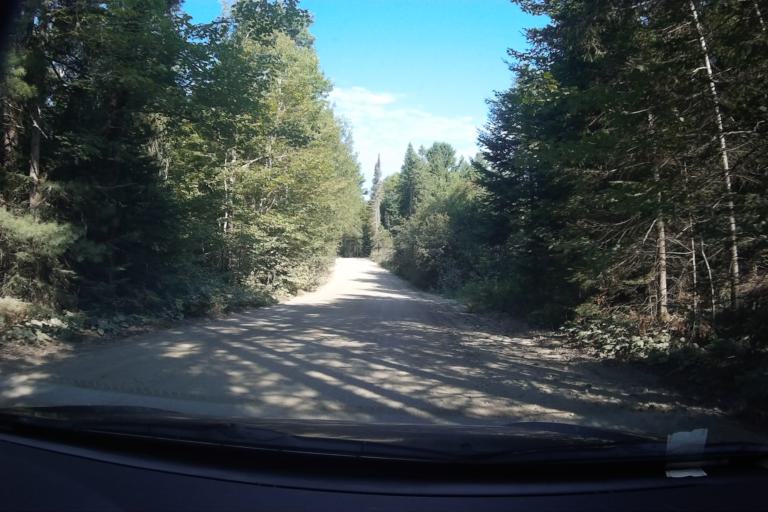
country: CA
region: Ontario
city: Huntsville
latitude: 45.5642
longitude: -78.7049
